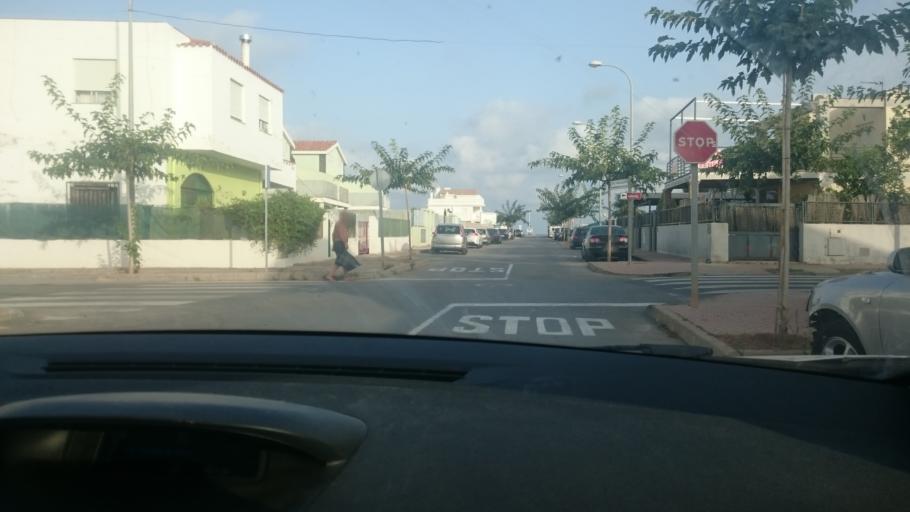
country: ES
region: Valencia
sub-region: Provincia de Castello
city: Moncofar
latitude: 39.7806
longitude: -0.1479
